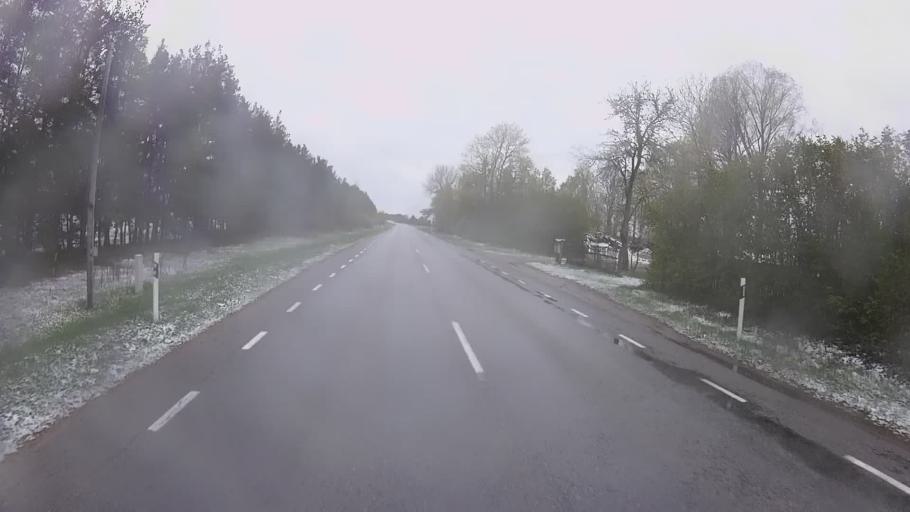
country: EE
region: Saare
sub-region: Kuressaare linn
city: Kuressaare
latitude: 58.5396
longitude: 22.6996
